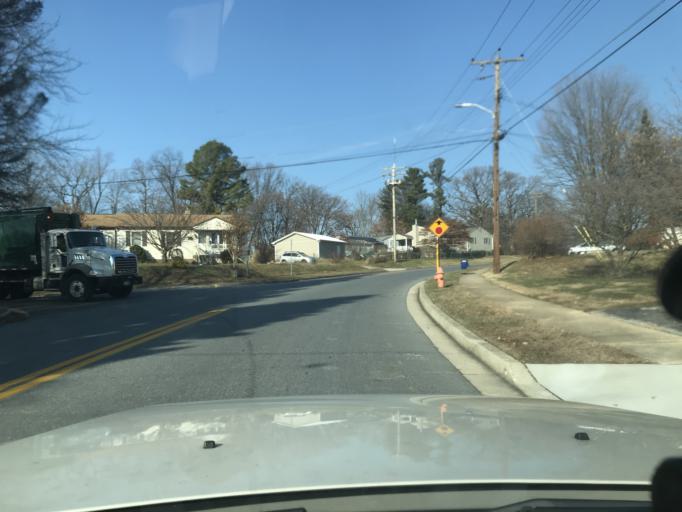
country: US
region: Maryland
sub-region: Baltimore County
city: Owings Mills
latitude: 39.4216
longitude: -76.7967
